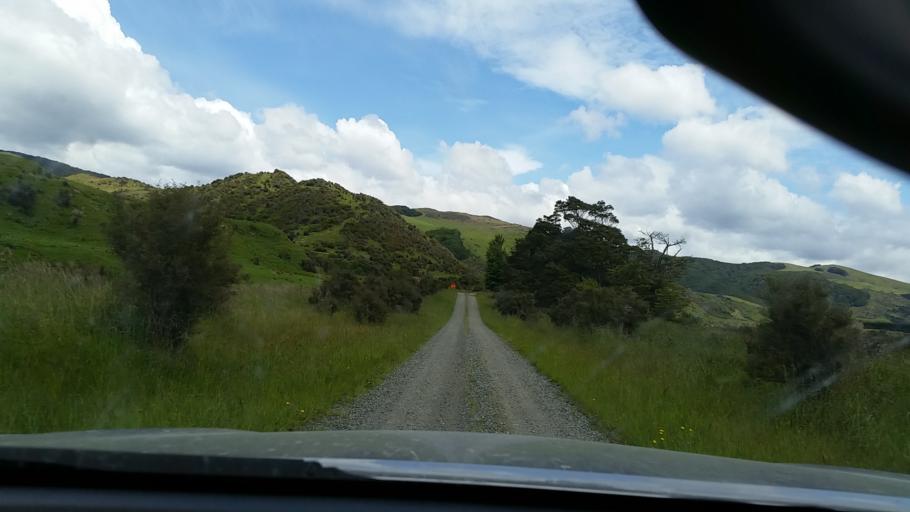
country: NZ
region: Southland
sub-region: Southland District
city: Te Anau
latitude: -45.7468
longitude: 168.0246
